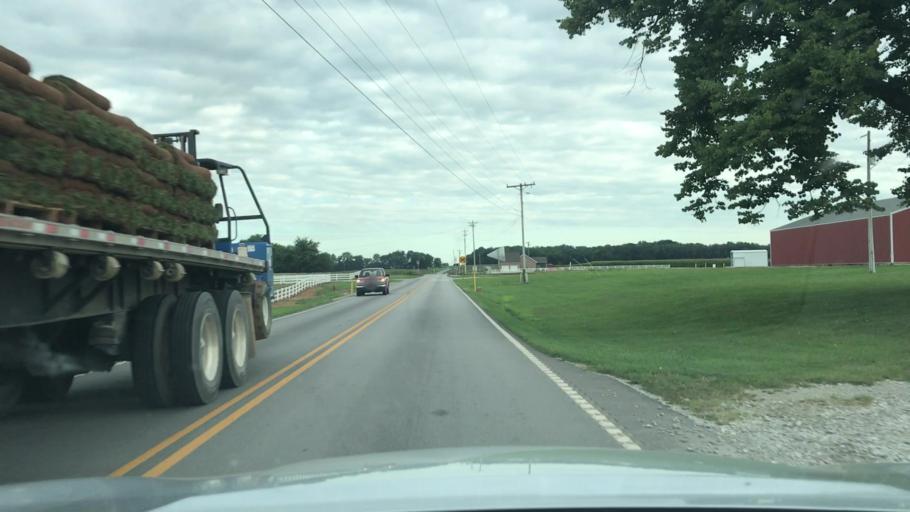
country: US
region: Kentucky
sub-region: Todd County
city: Guthrie
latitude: 36.6755
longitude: -87.1987
